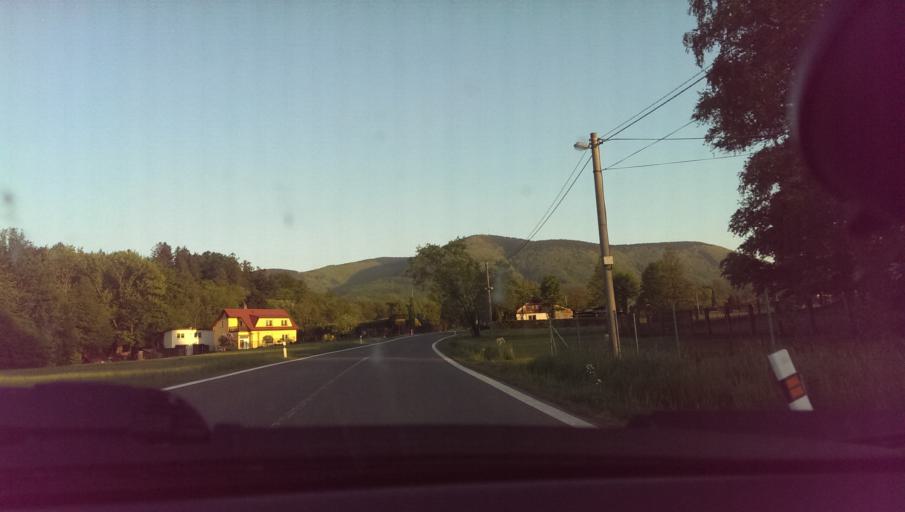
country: CZ
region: Moravskoslezsky
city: Frenstat pod Radhostem
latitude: 49.5301
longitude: 18.2043
